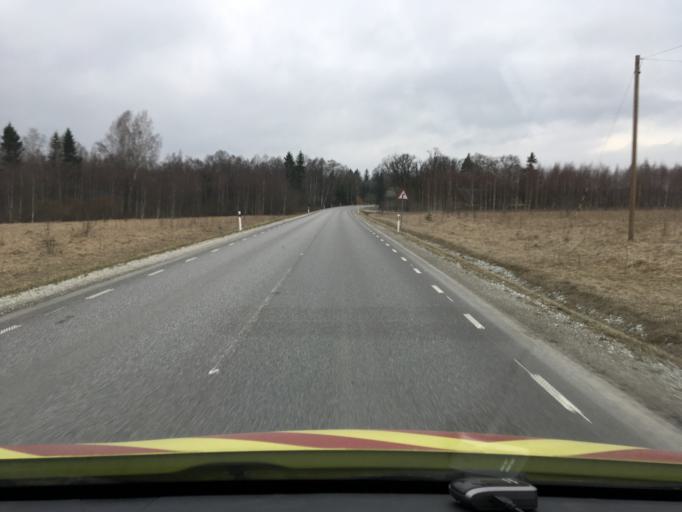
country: EE
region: Raplamaa
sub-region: Rapla vald
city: Rapla
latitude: 58.9976
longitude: 24.8453
